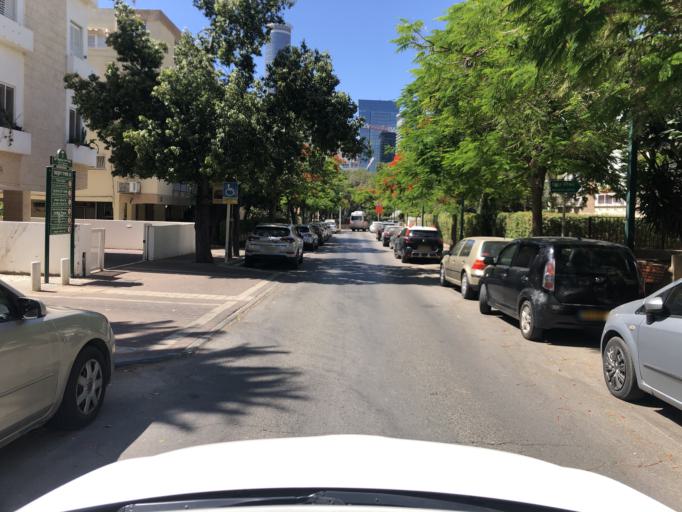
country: IL
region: Tel Aviv
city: Ramat Gan
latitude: 32.0774
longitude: 34.8062
